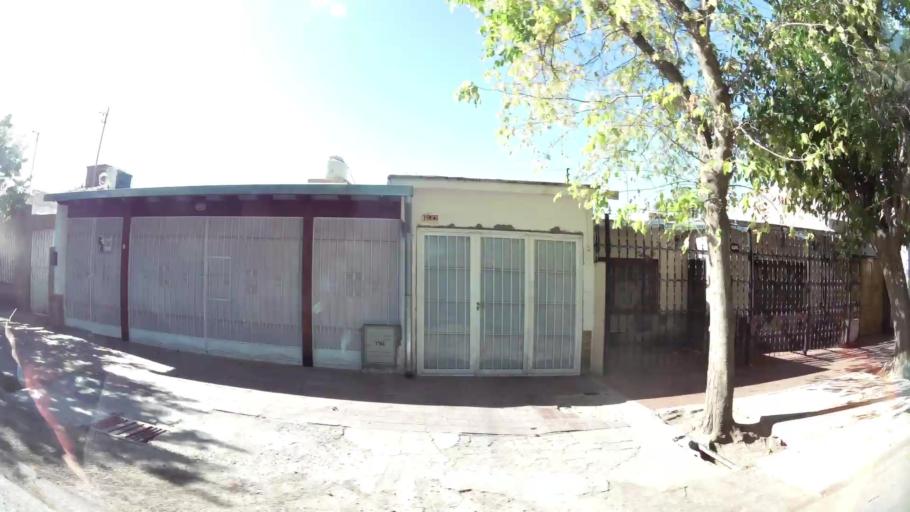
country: AR
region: Mendoza
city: Mendoza
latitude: -32.9040
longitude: -68.8161
